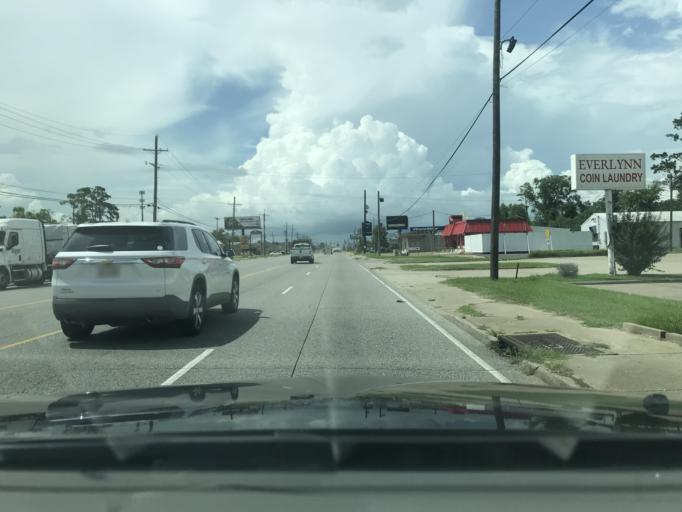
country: US
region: Louisiana
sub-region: Calcasieu Parish
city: Moss Bluff
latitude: 30.2554
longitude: -93.1806
